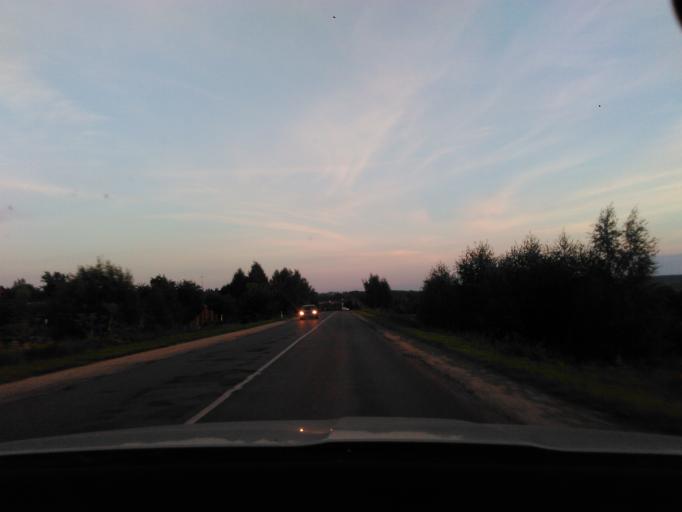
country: RU
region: Moskovskaya
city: Klin
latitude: 56.2826
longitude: 36.7776
